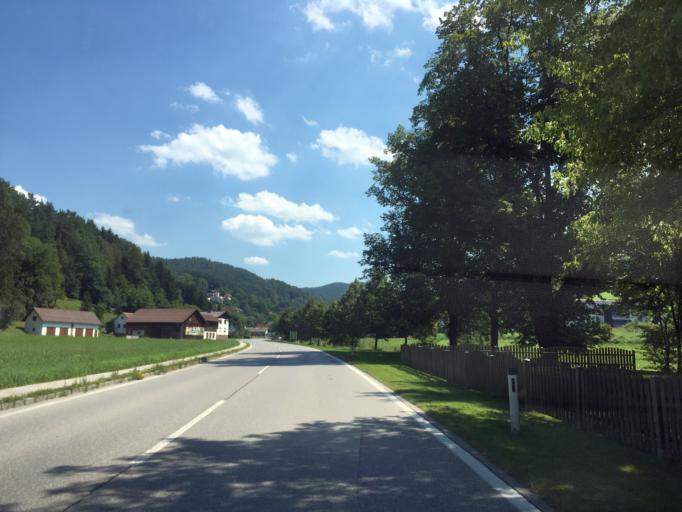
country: AT
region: Lower Austria
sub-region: Politischer Bezirk Neunkirchen
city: Grimmenstein
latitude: 47.6032
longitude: 16.1318
